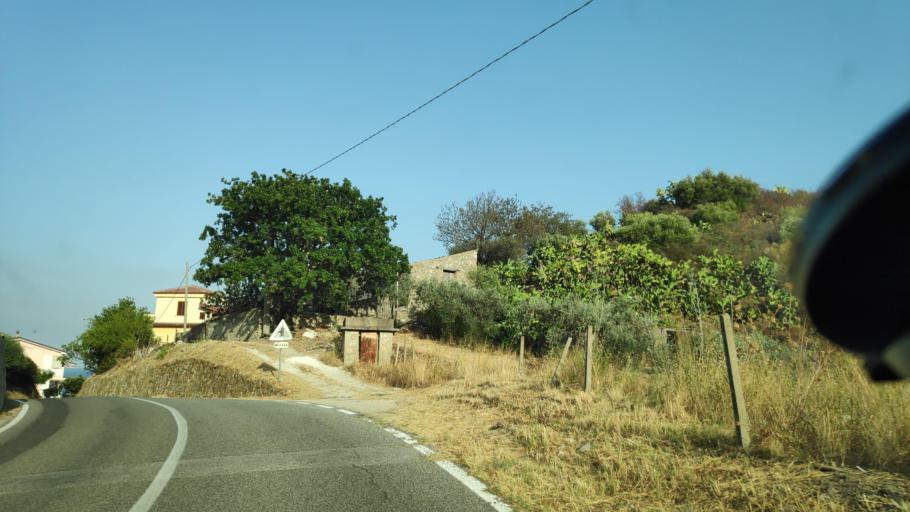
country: IT
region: Calabria
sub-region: Provincia di Catanzaro
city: Sant'Andrea Ionio Marina
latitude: 38.6204
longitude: 16.5414
